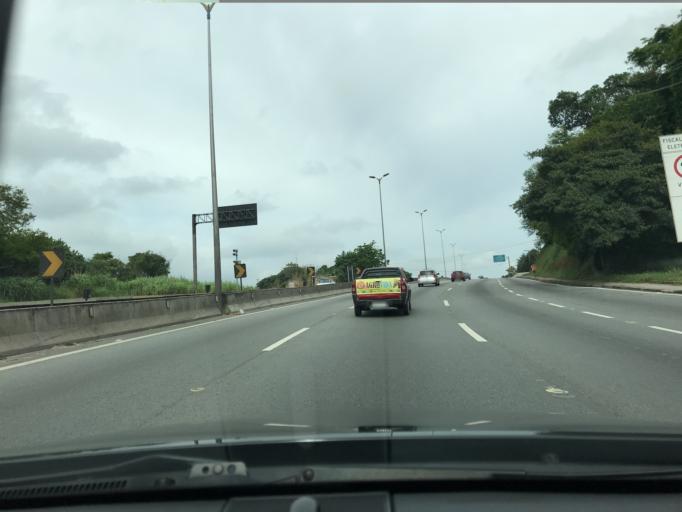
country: BR
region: Sao Paulo
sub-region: Cotia
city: Cotia
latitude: -23.6002
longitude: -46.8837
